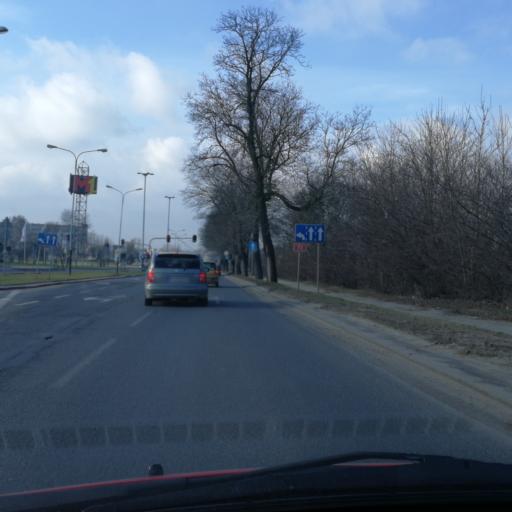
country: PL
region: Lodz Voivodeship
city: Lodz
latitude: 51.7968
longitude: 19.5170
